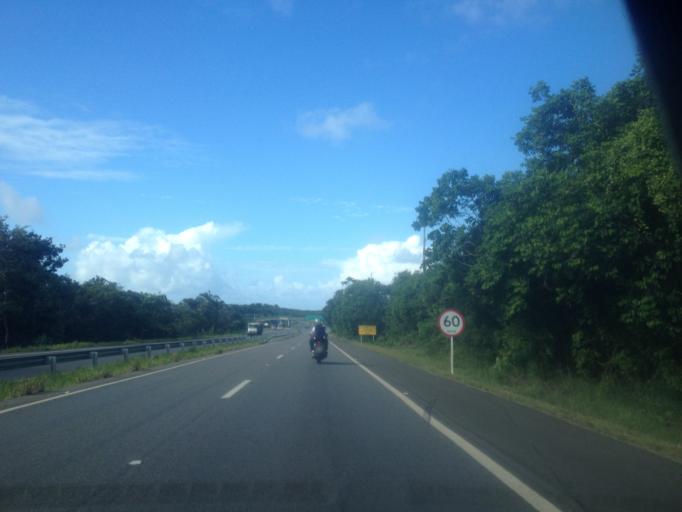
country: BR
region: Bahia
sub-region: Mata De Sao Joao
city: Mata de Sao Joao
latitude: -12.5645
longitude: -38.0213
